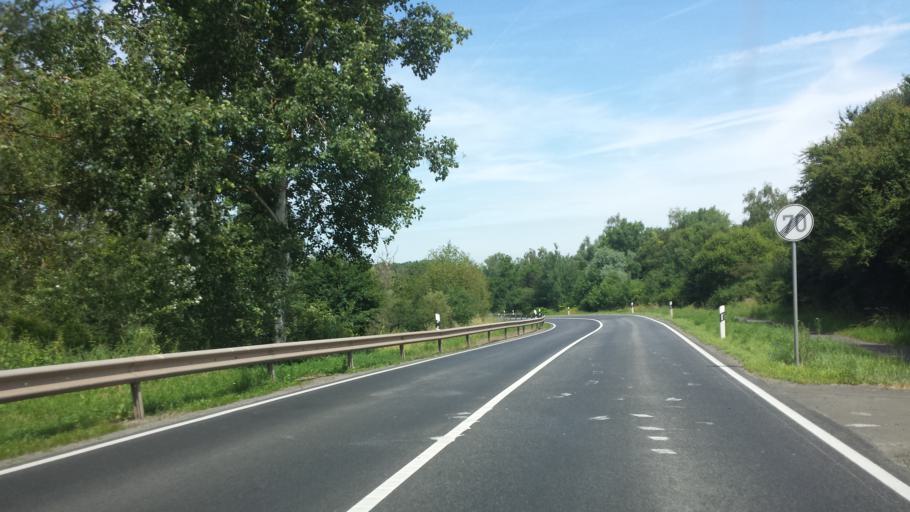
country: DE
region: Rheinland-Pfalz
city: Hettenleidelheim
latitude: 49.5422
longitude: 8.0737
